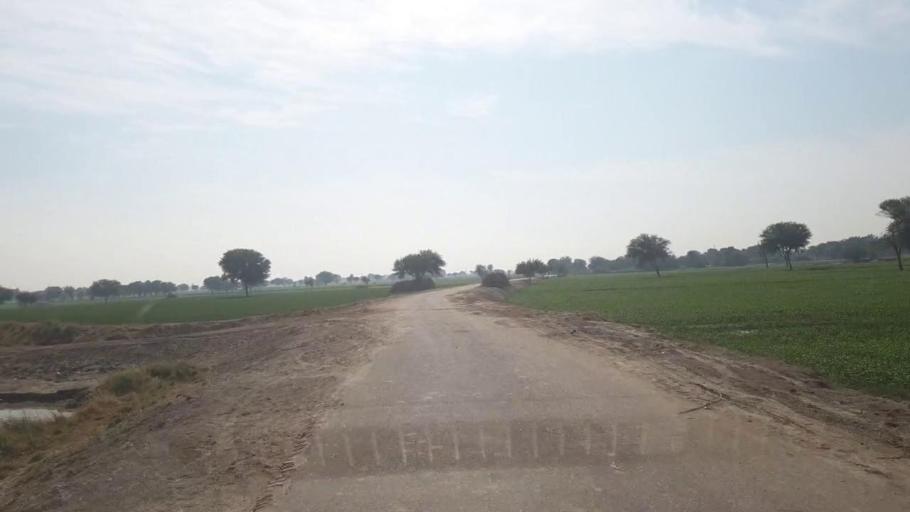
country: PK
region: Sindh
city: Shahpur Chakar
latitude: 26.1550
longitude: 68.5150
